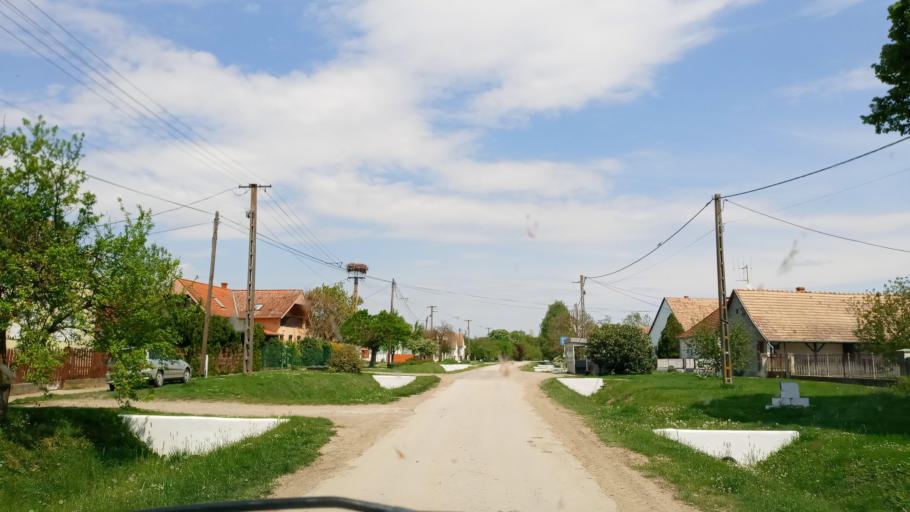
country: HU
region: Baranya
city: Villany
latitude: 45.8187
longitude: 18.4950
